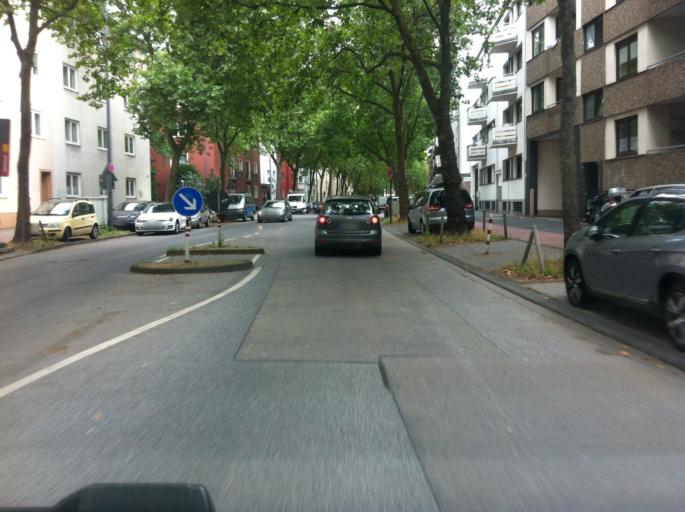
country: DE
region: North Rhine-Westphalia
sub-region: Regierungsbezirk Koln
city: Neuehrenfeld
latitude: 50.9384
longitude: 6.8998
